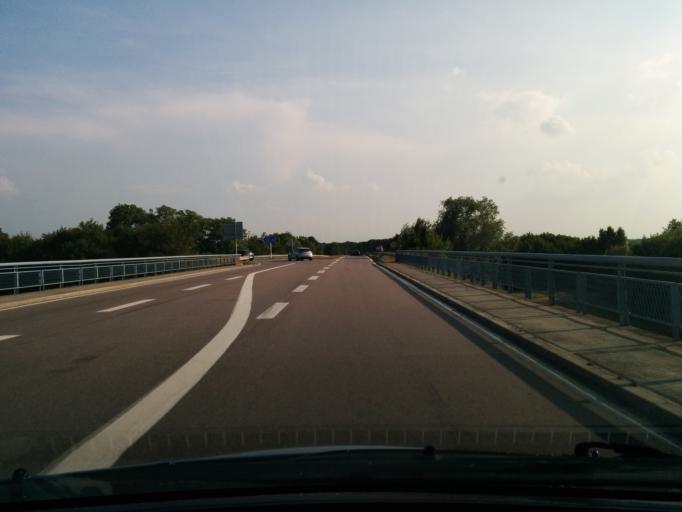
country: FR
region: Haute-Normandie
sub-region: Departement de l'Eure
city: Saint-Aubin-sur-Gaillon
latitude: 49.1355
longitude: 1.3133
